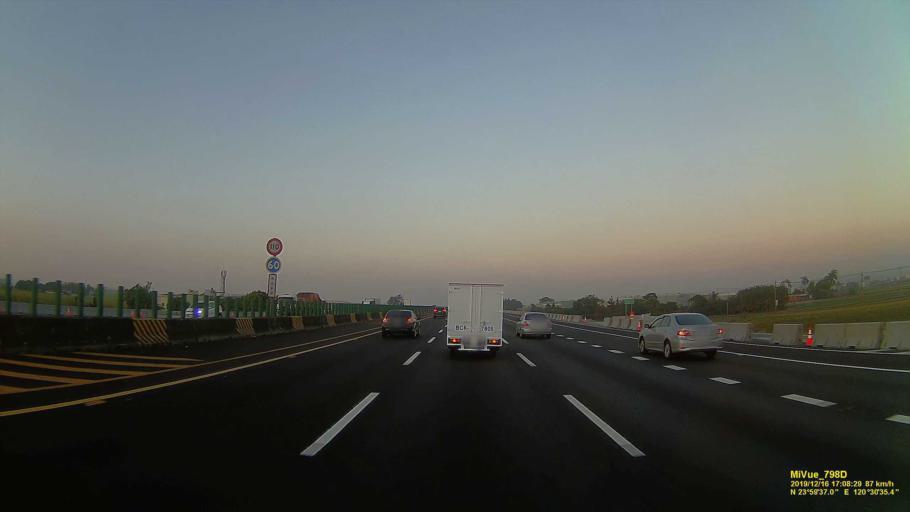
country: TW
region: Taiwan
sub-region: Changhua
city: Chang-hua
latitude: 23.9940
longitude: 120.5097
